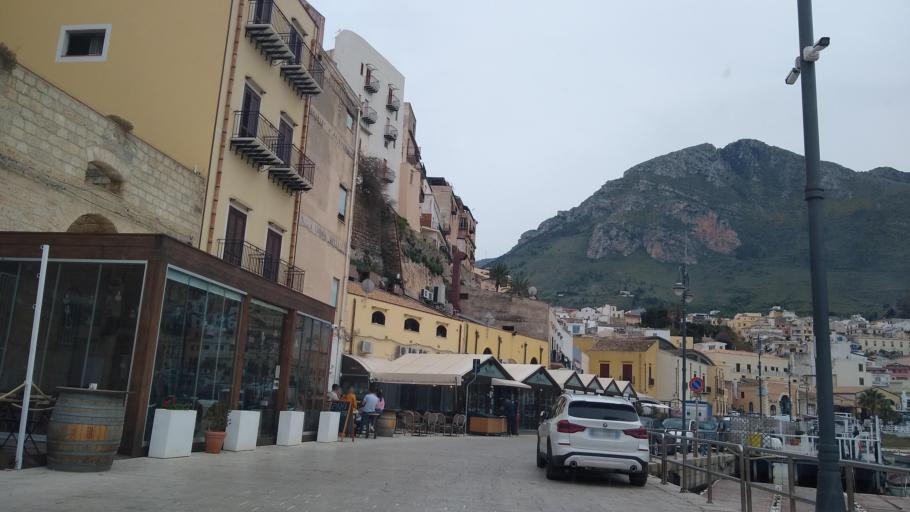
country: IT
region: Sicily
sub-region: Trapani
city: Castellammare del Golfo
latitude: 38.0297
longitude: 12.8813
